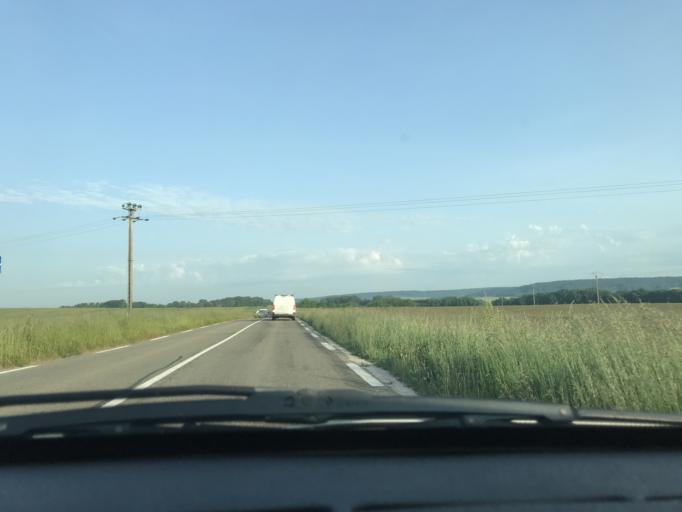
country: FR
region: Lorraine
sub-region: Departement de la Moselle
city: Vic-sur-Seille
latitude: 48.7787
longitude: 6.5026
